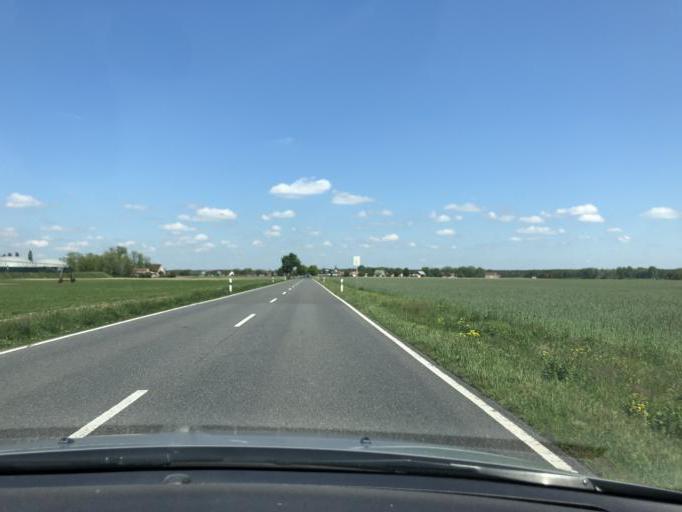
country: DE
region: Saxony
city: Arzberg
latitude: 51.6070
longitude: 13.1360
